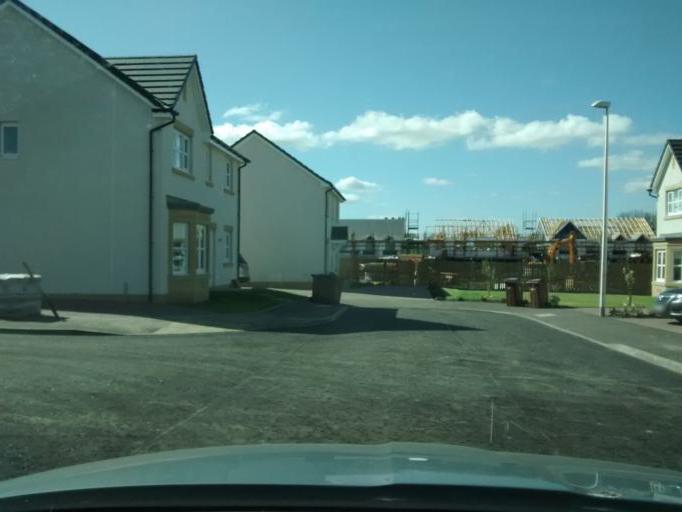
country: GB
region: Scotland
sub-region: West Lothian
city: Broxburn
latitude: 55.9591
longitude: -3.4765
